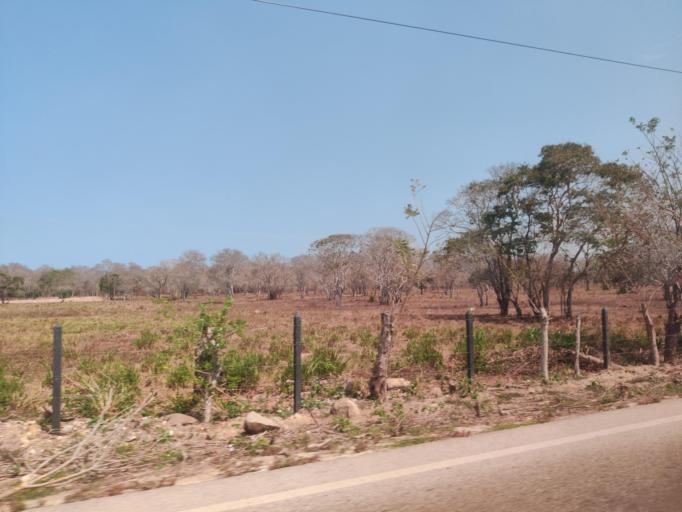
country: CO
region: Bolivar
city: Turbana
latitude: 10.2107
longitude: -75.6058
